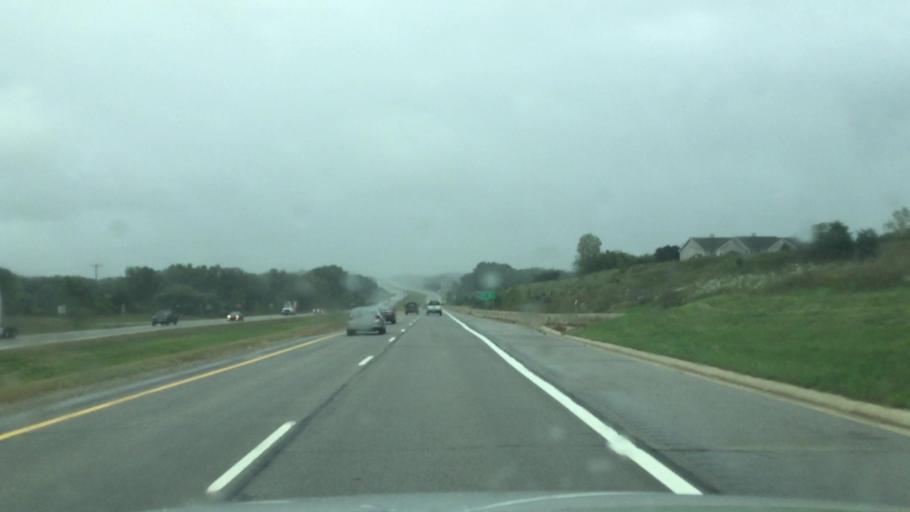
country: US
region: Michigan
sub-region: Livingston County
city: Howell
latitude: 42.6222
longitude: -83.9726
